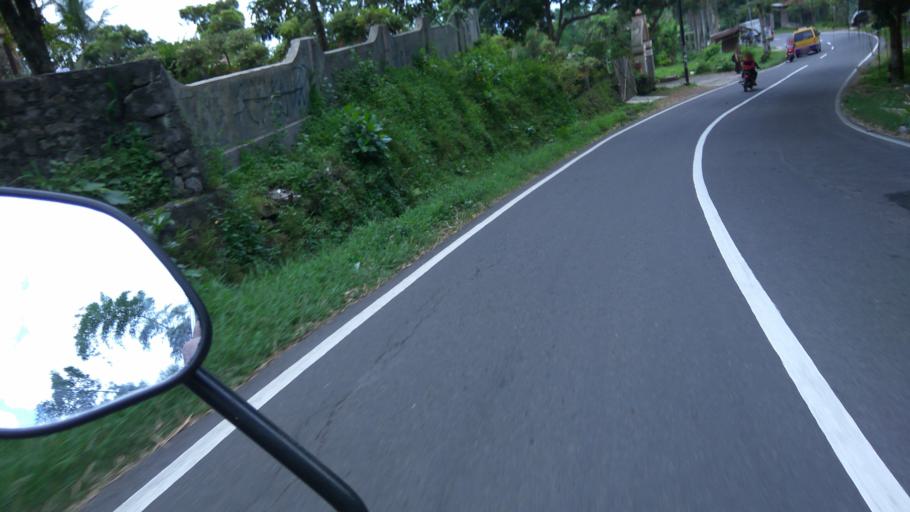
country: ID
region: Central Java
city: Ambarawa
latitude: -7.2359
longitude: 110.3849
